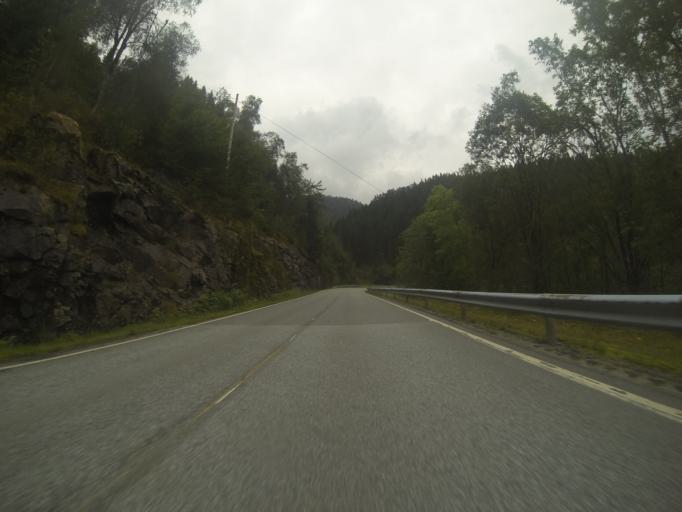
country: NO
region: Rogaland
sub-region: Suldal
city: Sand
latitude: 59.5564
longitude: 6.2614
